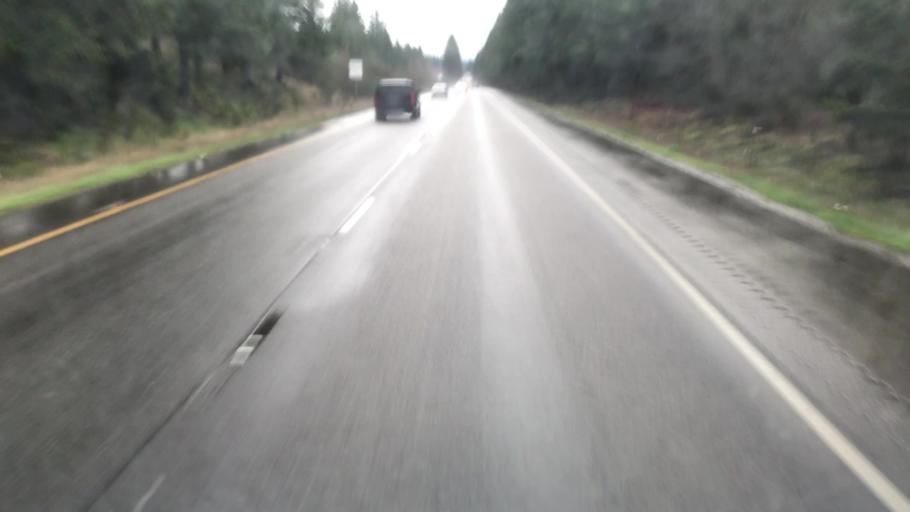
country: US
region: Washington
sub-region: Kitsap County
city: Burley
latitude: 47.4480
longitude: -122.6222
